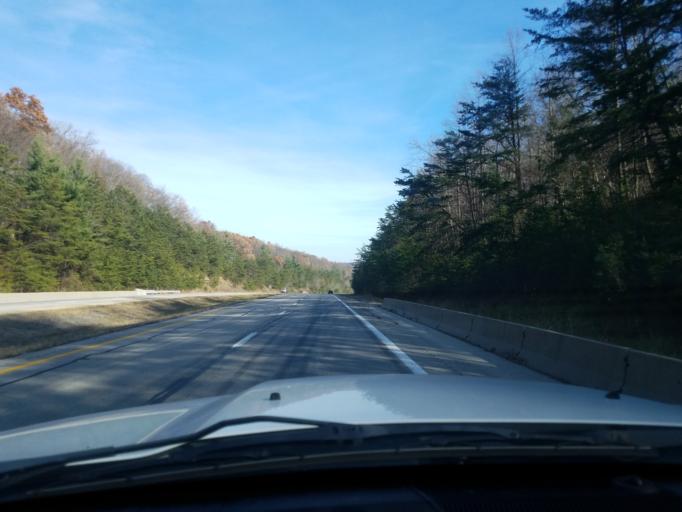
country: US
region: Ohio
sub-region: Adams County
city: Peebles
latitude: 39.0219
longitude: -83.2759
